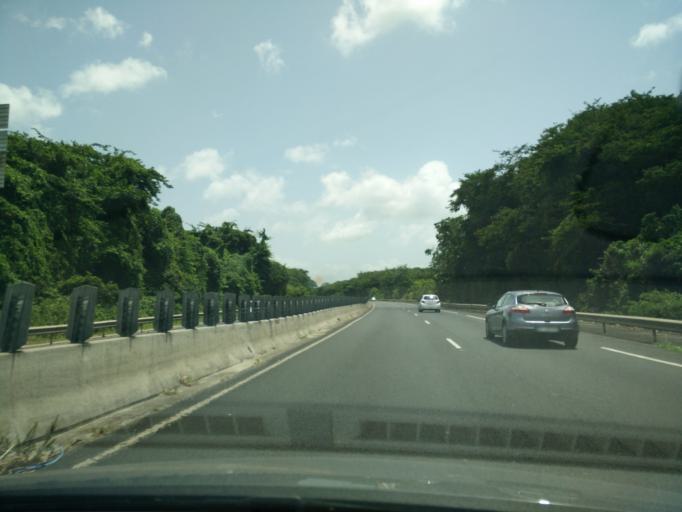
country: GP
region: Guadeloupe
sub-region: Guadeloupe
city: Les Abymes
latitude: 16.2759
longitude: -61.5291
